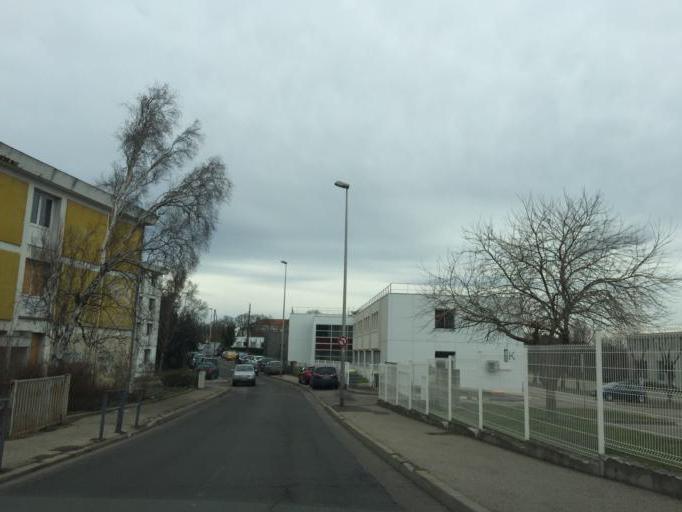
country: FR
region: Rhone-Alpes
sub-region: Departement de la Loire
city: Saint-Etienne
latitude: 45.4235
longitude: 4.4247
